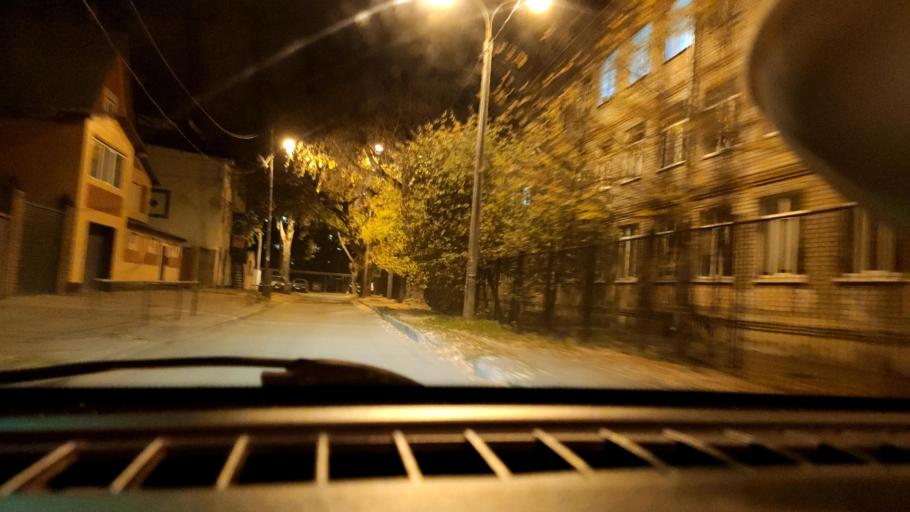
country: RU
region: Samara
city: Samara
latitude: 53.2024
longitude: 50.1859
